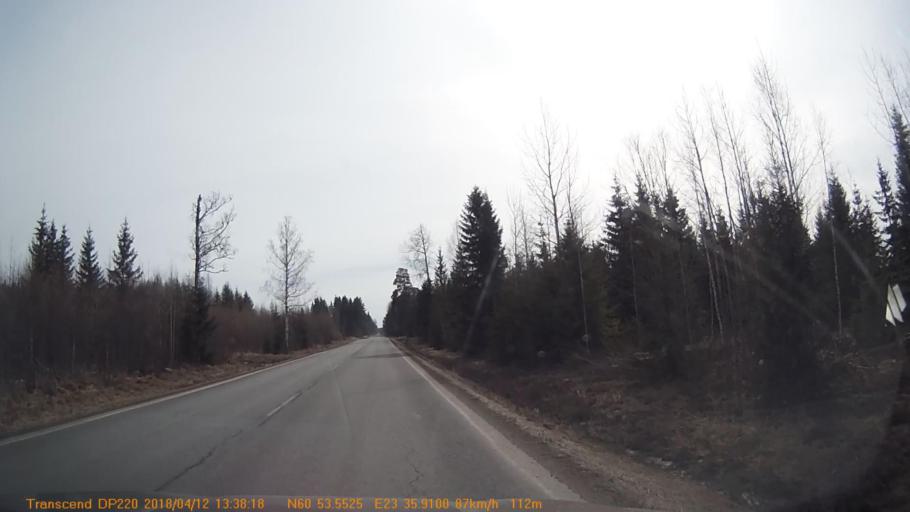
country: FI
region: Haeme
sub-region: Forssa
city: Forssa
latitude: 60.8922
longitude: 23.5986
